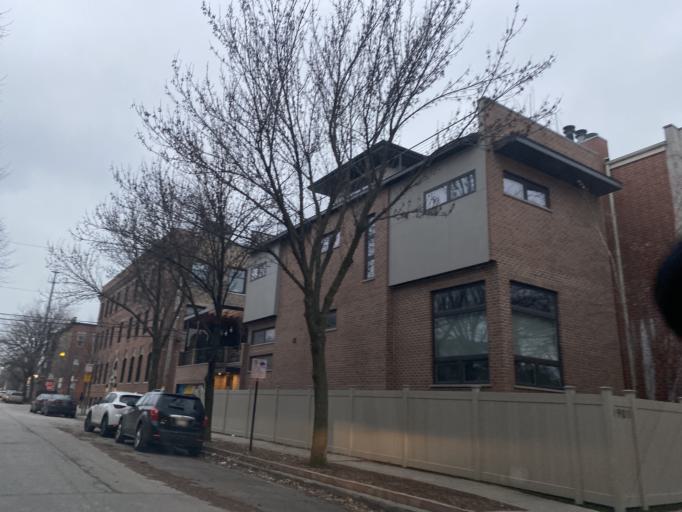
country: US
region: Illinois
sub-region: Cook County
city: Chicago
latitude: 41.8923
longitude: -87.6745
